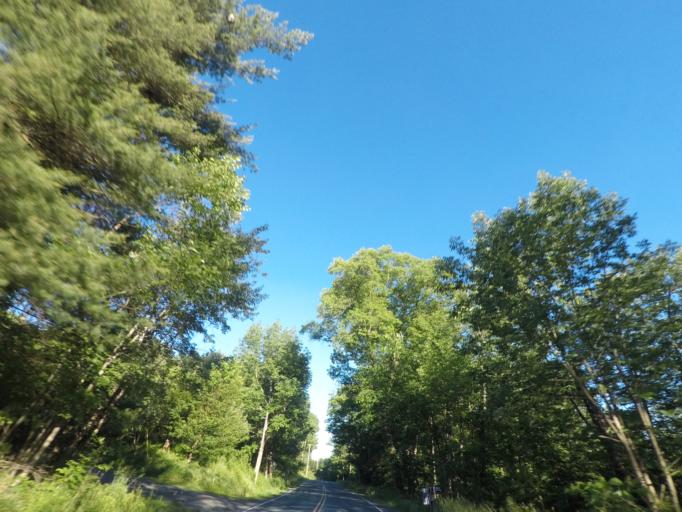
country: US
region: New York
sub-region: Rensselaer County
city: Averill Park
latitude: 42.5896
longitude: -73.5815
